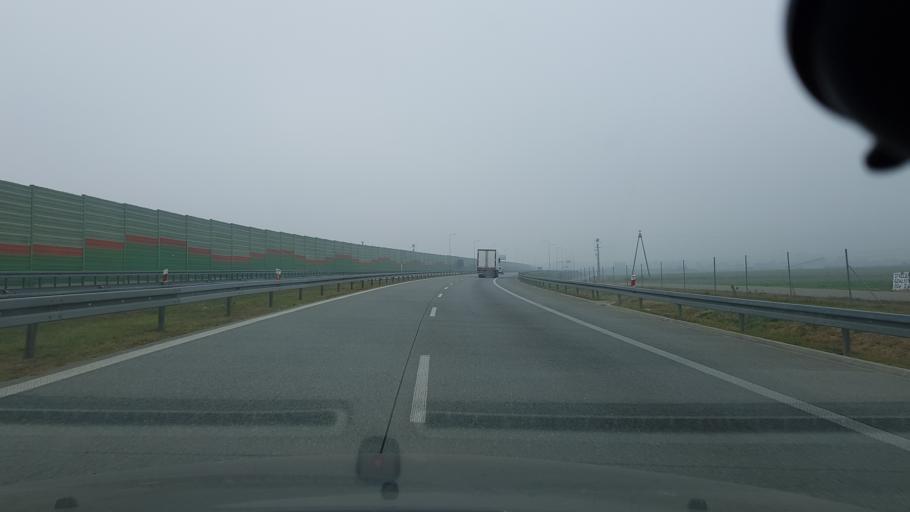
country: PL
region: Lodz Voivodeship
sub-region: Powiat tomaszowski
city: Czerniewice
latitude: 51.6600
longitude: 20.1649
